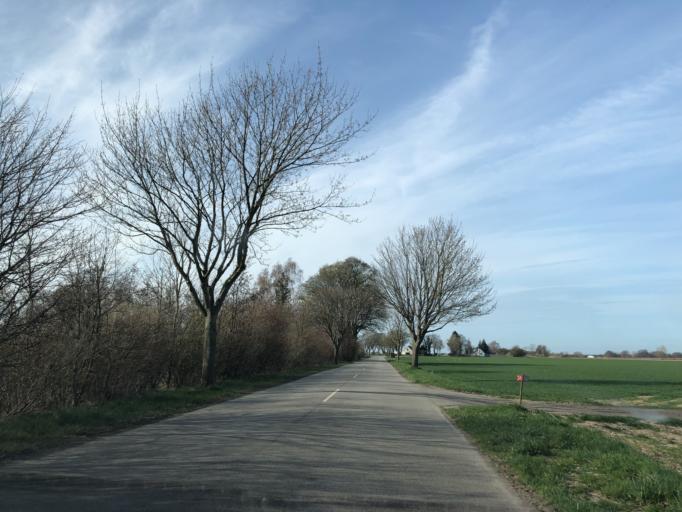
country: DK
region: Zealand
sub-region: Stevns Kommune
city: Store Heddinge
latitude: 55.3123
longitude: 12.4358
